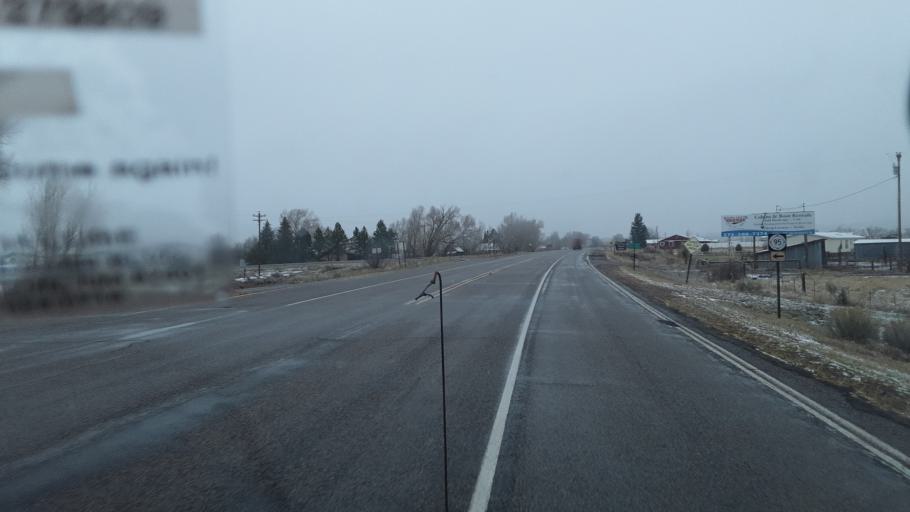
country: US
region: New Mexico
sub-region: Rio Arriba County
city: Tierra Amarilla
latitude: 36.7366
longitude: -106.5682
